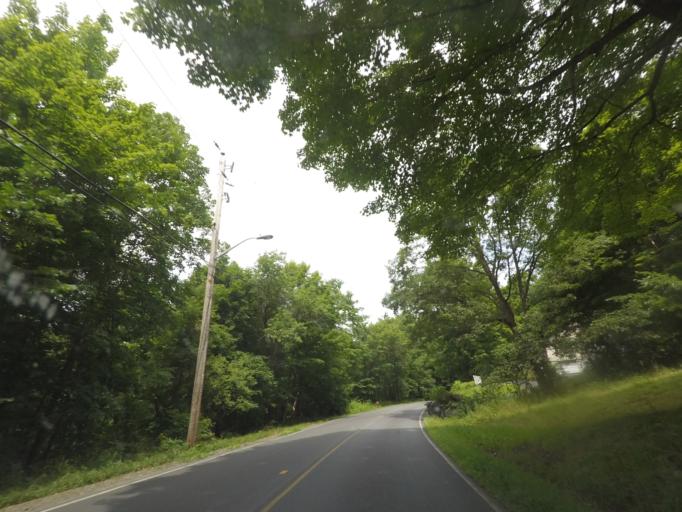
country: US
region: New York
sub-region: Rensselaer County
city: Wynantskill
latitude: 42.6935
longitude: -73.6284
